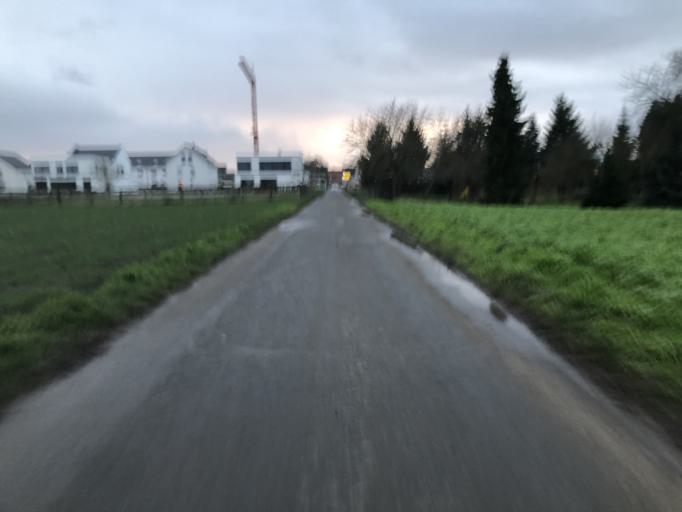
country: DE
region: Baden-Wuerttemberg
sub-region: Karlsruhe Region
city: Reilingen
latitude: 49.2984
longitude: 8.5747
